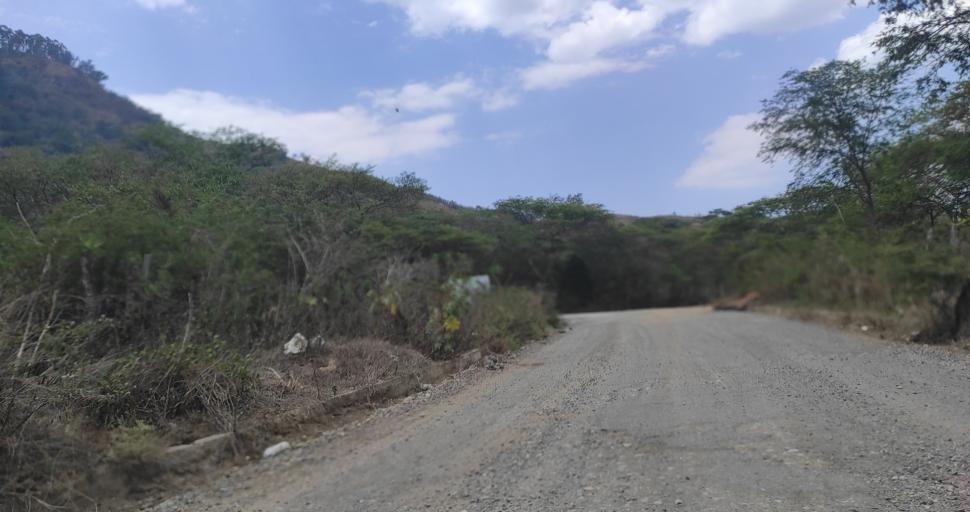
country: EC
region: Loja
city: Catacocha
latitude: -4.0299
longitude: -79.6437
